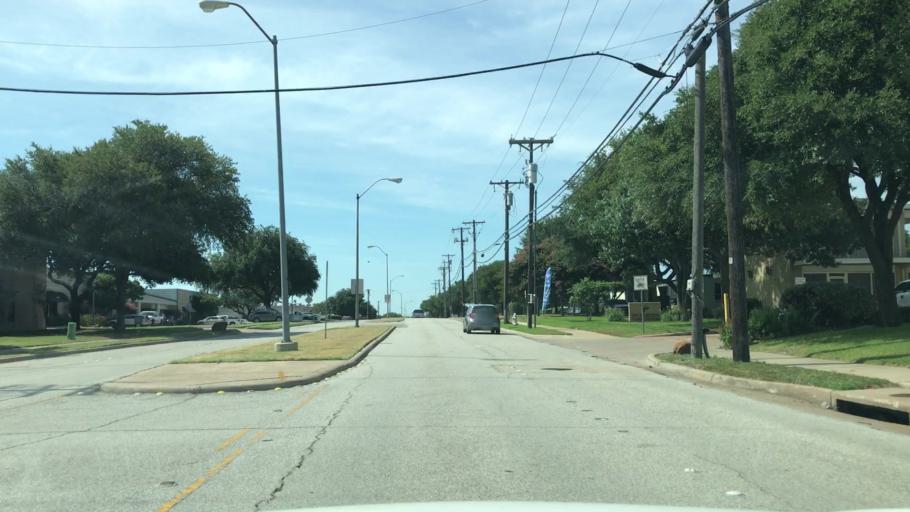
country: US
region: Texas
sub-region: Dallas County
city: Richardson
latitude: 32.9588
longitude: -96.7138
